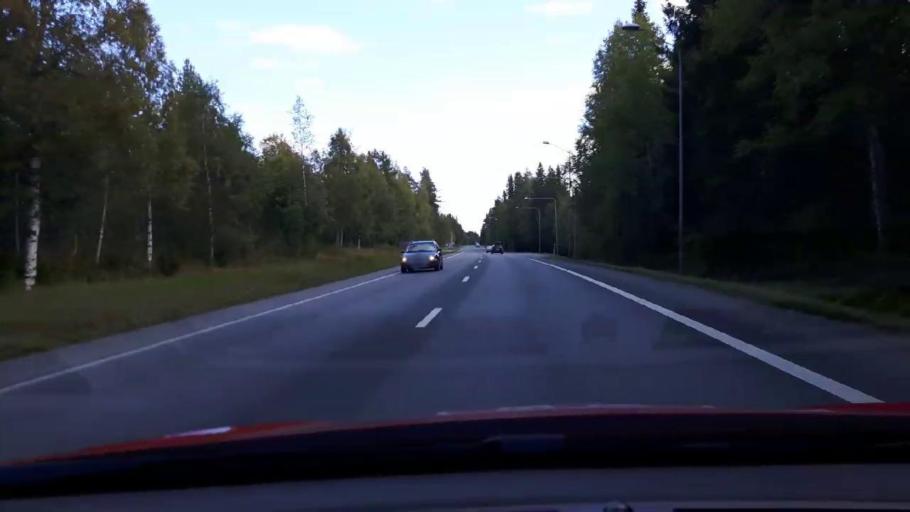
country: SE
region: Jaemtland
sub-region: OEstersunds Kommun
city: Brunflo
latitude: 63.0926
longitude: 14.8032
